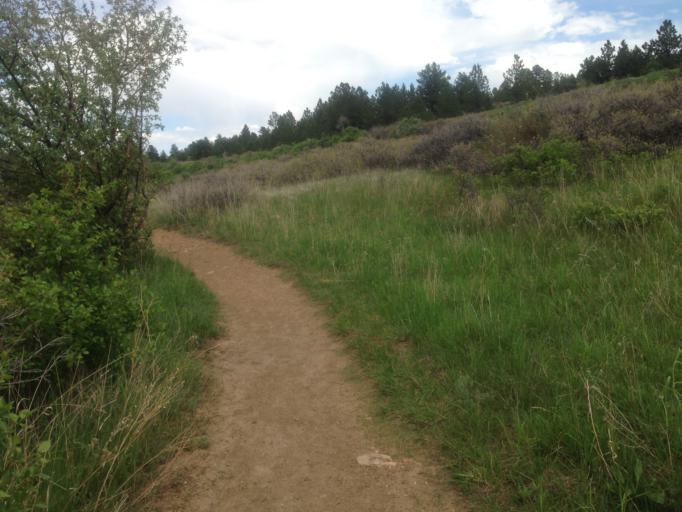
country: US
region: Colorado
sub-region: Boulder County
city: Superior
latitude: 39.9490
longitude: -105.2260
